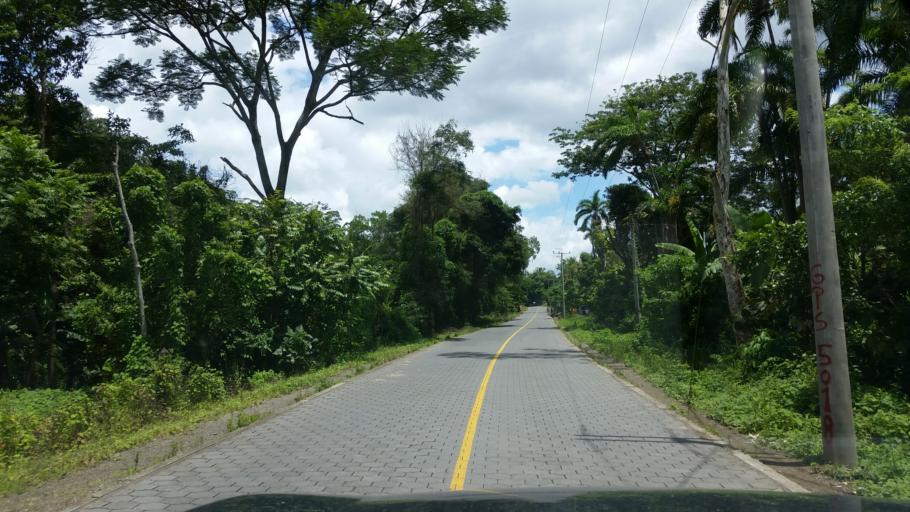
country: NI
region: Atlantico Norte (RAAN)
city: Waslala
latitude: 13.2475
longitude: -85.6145
